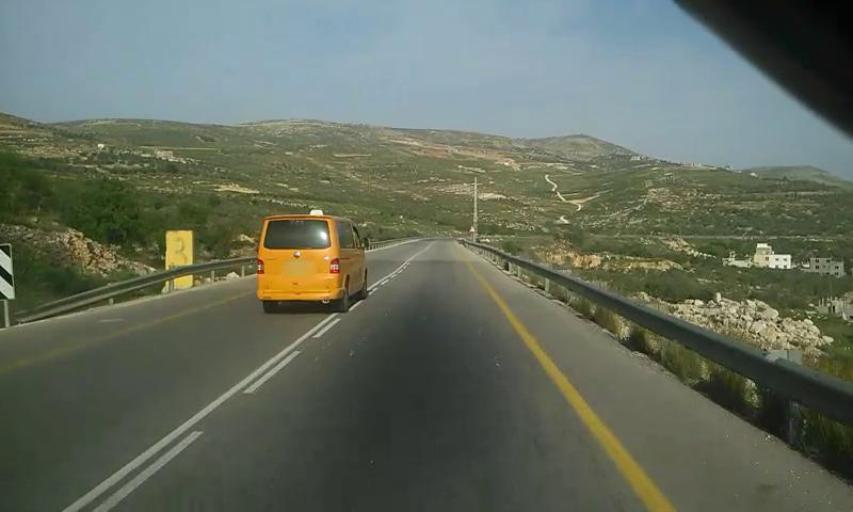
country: PS
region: West Bank
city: Madama
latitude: 32.1892
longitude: 35.2254
